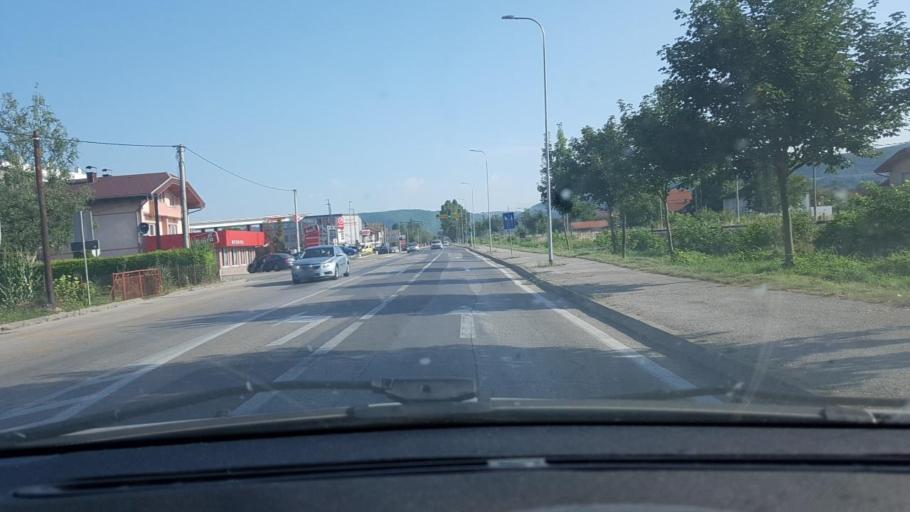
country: BA
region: Federation of Bosnia and Herzegovina
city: Bihac
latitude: 44.8310
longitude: 15.8818
